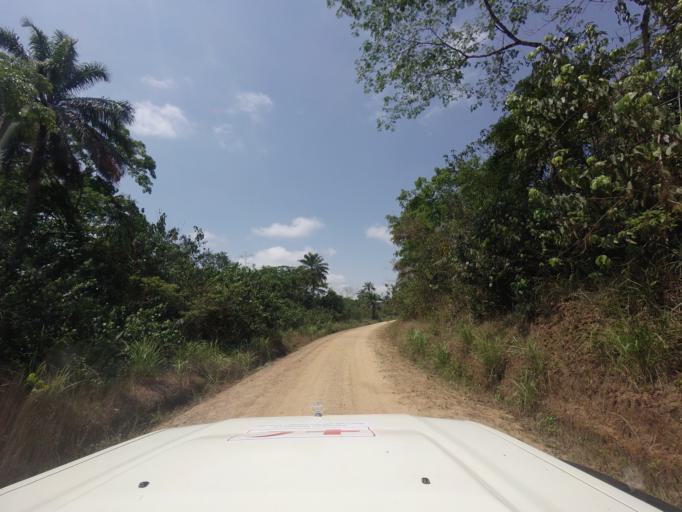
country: LR
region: Lofa
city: Voinjama
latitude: 8.4890
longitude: -9.6558
